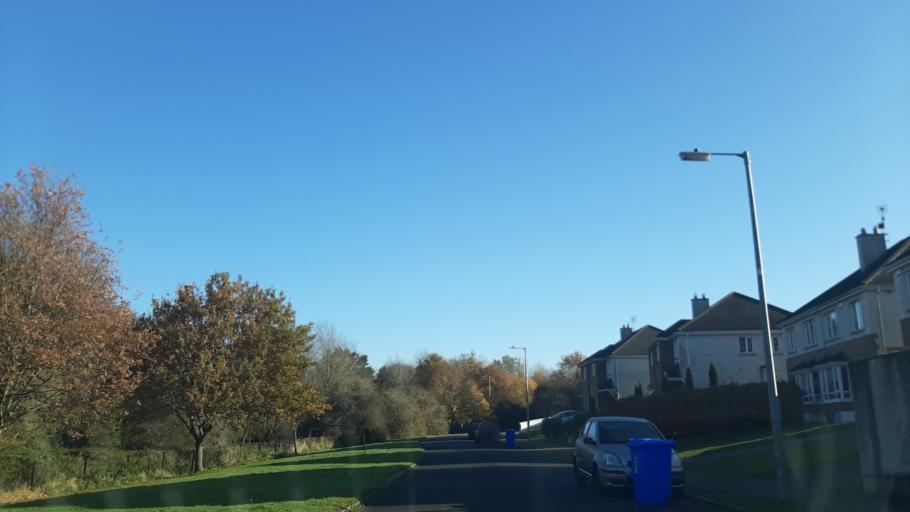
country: IE
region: Leinster
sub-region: Kildare
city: Rathangan
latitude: 53.2193
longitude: -6.9976
